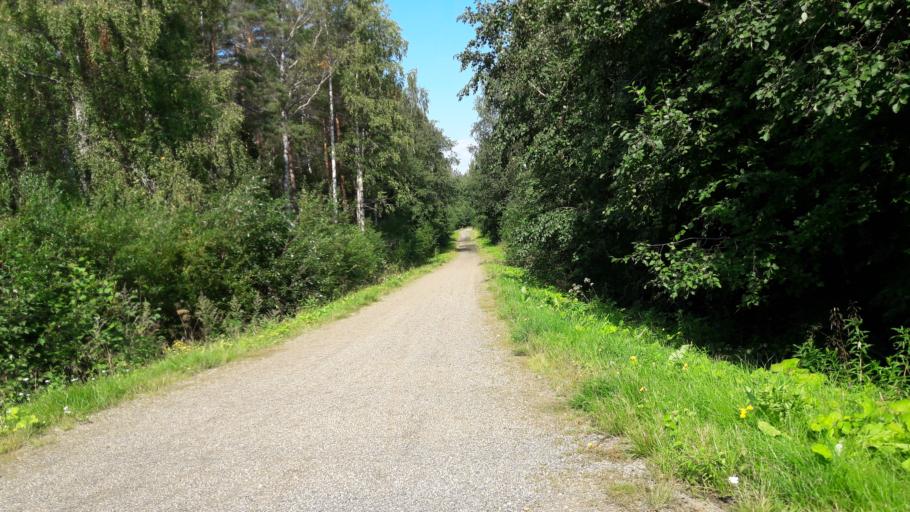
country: FI
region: North Karelia
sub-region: Joensuu
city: Joensuu
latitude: 62.5310
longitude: 29.8498
